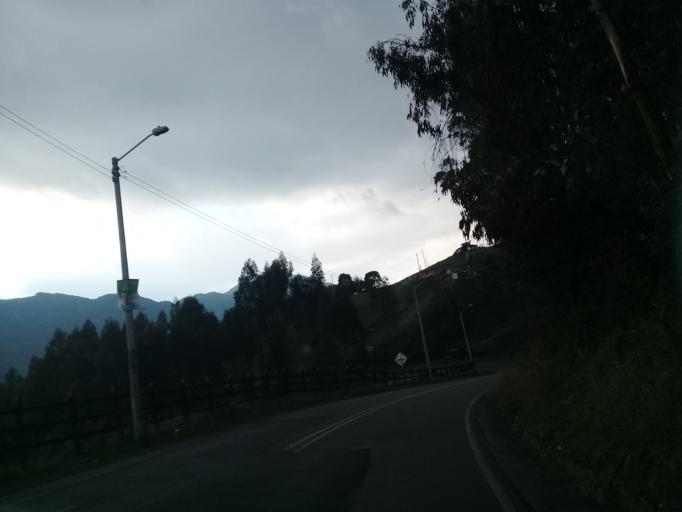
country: CO
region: Cundinamarca
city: Zipaquira
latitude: 5.0541
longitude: -74.0544
